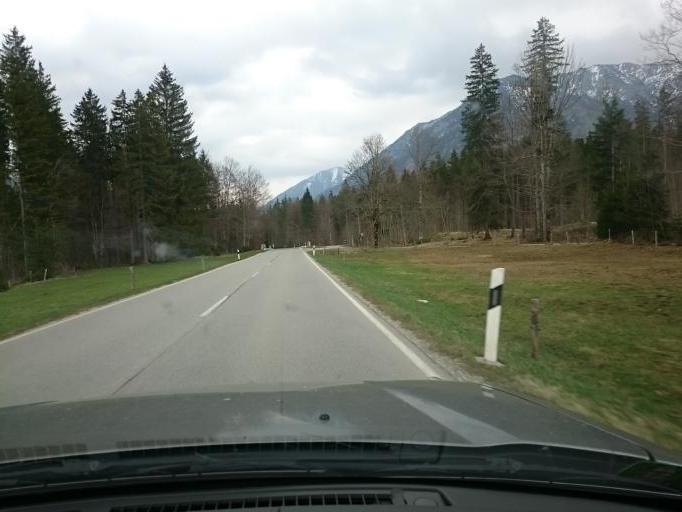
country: DE
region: Bavaria
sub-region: Upper Bavaria
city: Unterammergau
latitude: 47.5651
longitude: 10.9665
